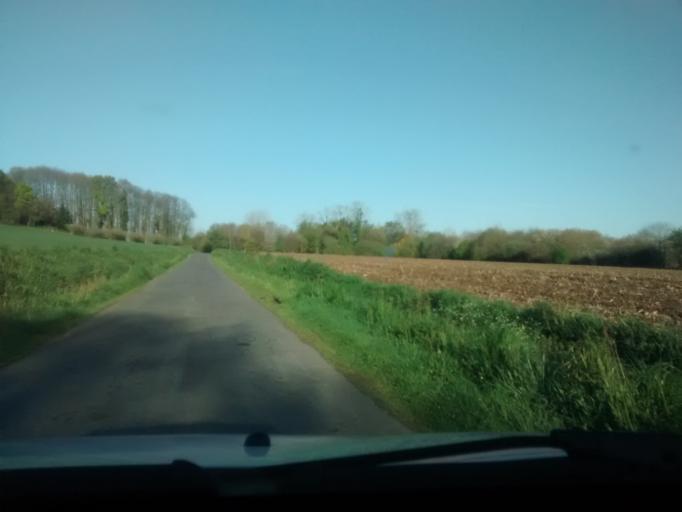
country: FR
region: Brittany
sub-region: Departement d'Ille-et-Vilaine
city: Roz-sur-Couesnon
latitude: 48.5530
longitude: -1.5978
